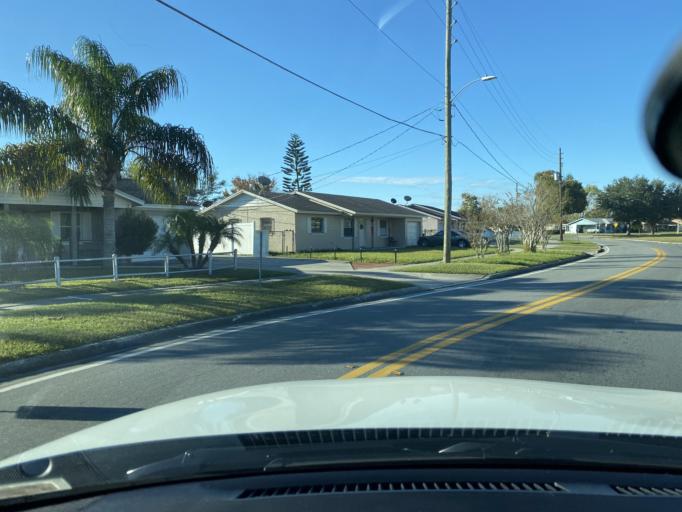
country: US
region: Florida
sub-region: Orange County
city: Azalea Park
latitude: 28.5264
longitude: -81.2988
